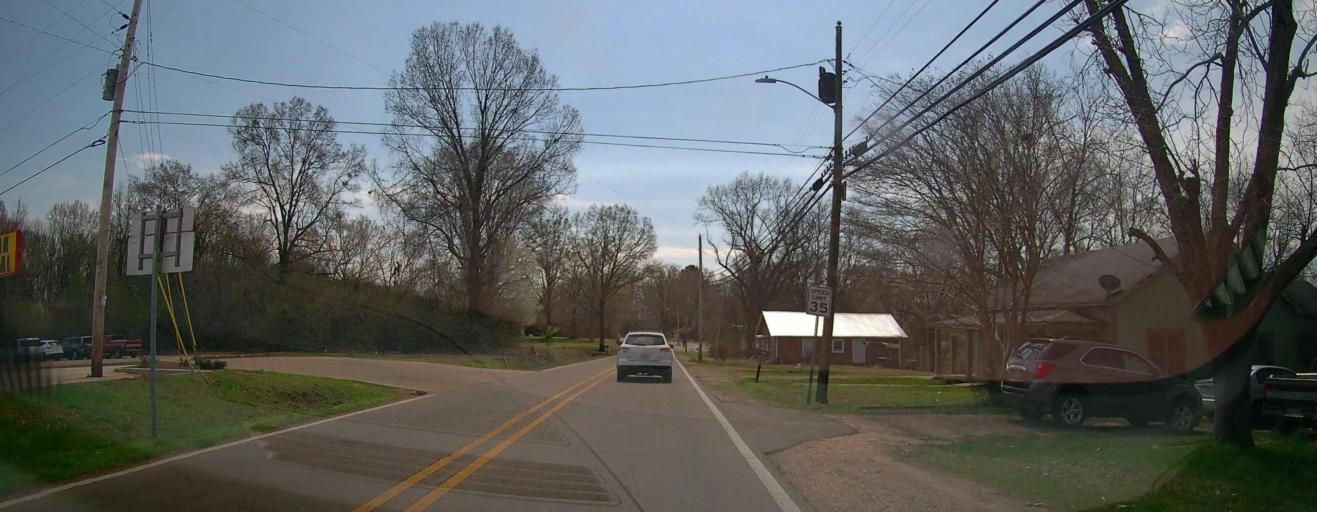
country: US
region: Mississippi
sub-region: Union County
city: New Albany
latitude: 34.4807
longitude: -88.9990
